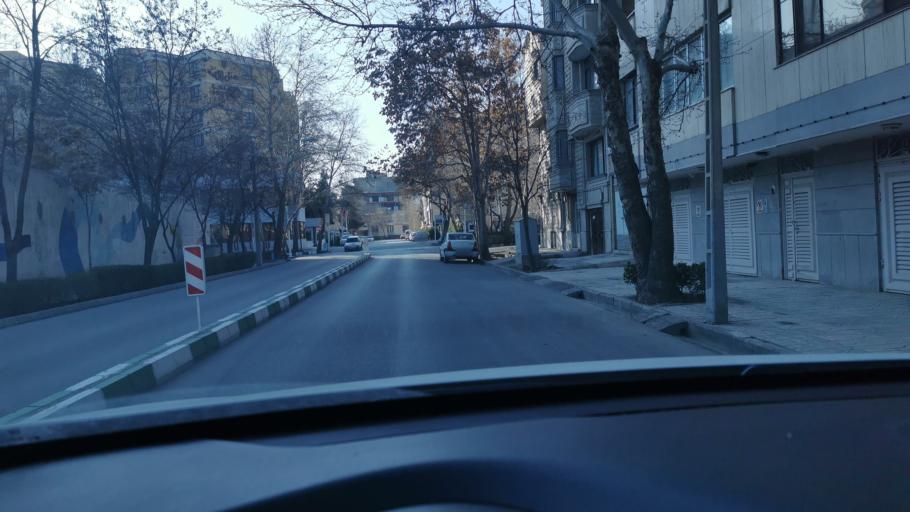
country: IR
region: Razavi Khorasan
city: Mashhad
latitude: 36.2854
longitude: 59.5675
